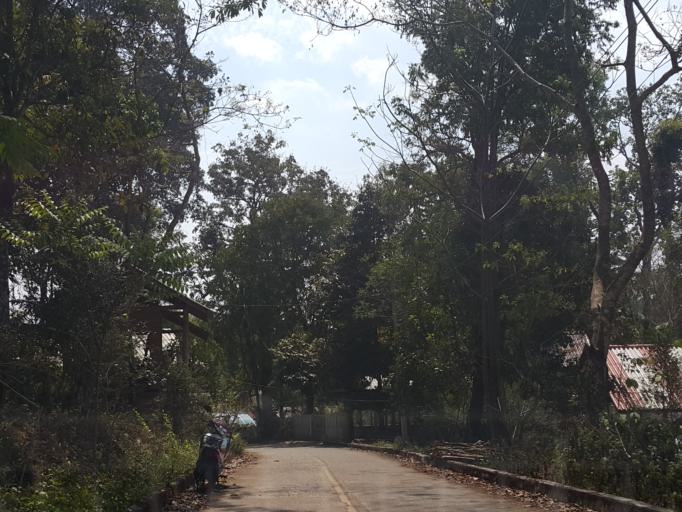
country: TH
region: Lampang
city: Mueang Pan
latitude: 18.8304
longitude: 99.3836
